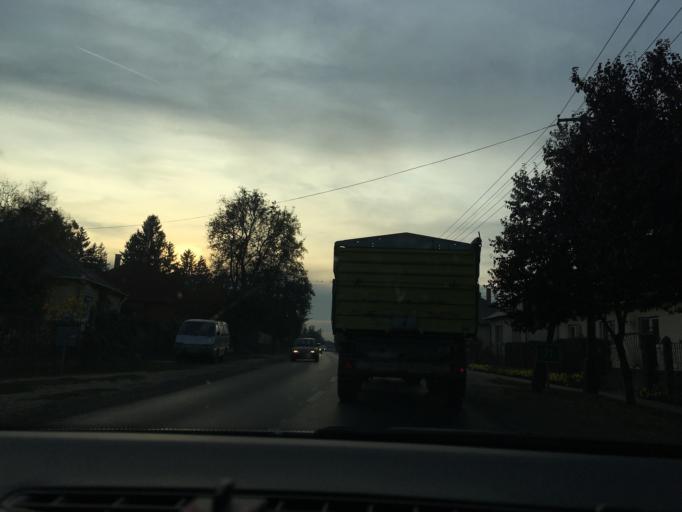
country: HU
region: Szabolcs-Szatmar-Bereg
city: Kallosemjen
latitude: 47.8592
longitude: 21.9365
